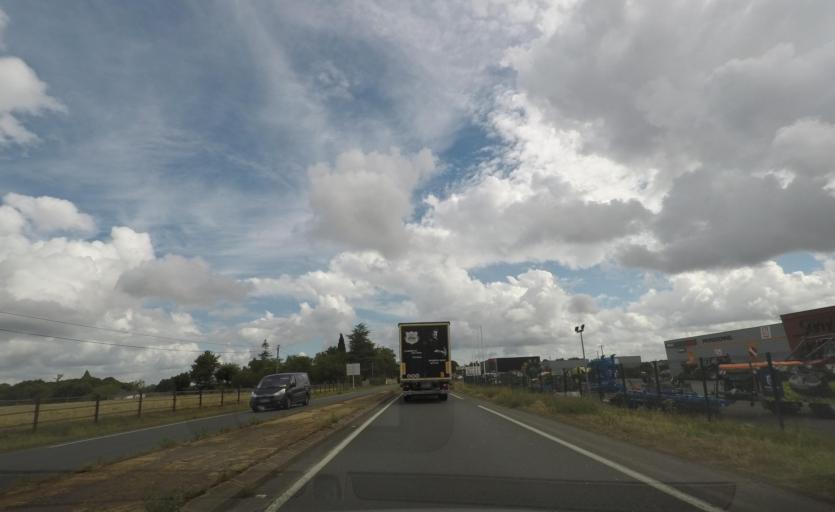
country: FR
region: Pays de la Loire
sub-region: Departement de Maine-et-Loire
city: Corze
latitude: 47.5554
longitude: -0.3805
